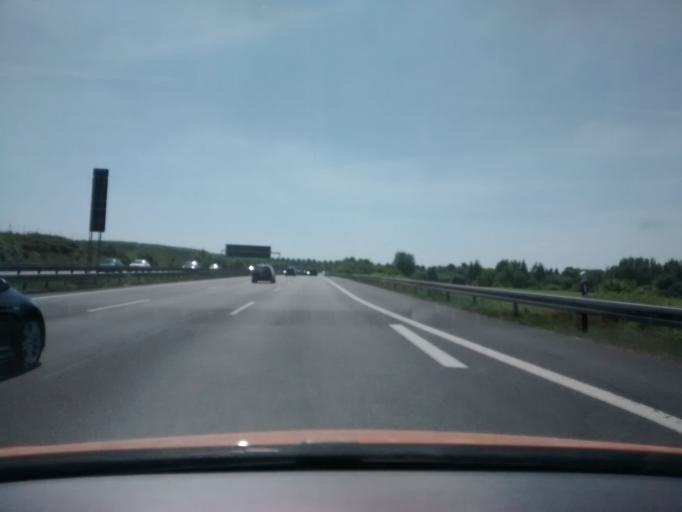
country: DE
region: Brandenburg
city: Schulzendorf
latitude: 52.3530
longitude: 13.5518
